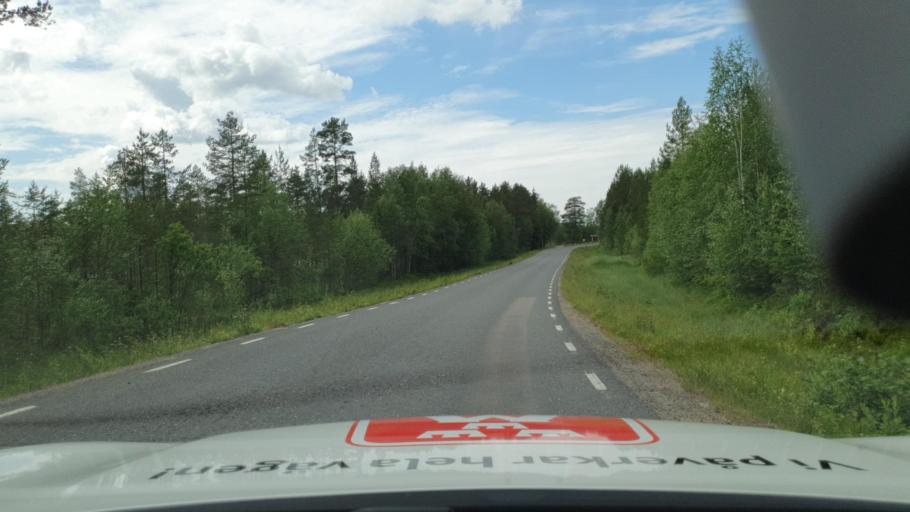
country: NO
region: Hedmark
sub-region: Grue
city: Kirkenaer
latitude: 60.6799
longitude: 12.6629
